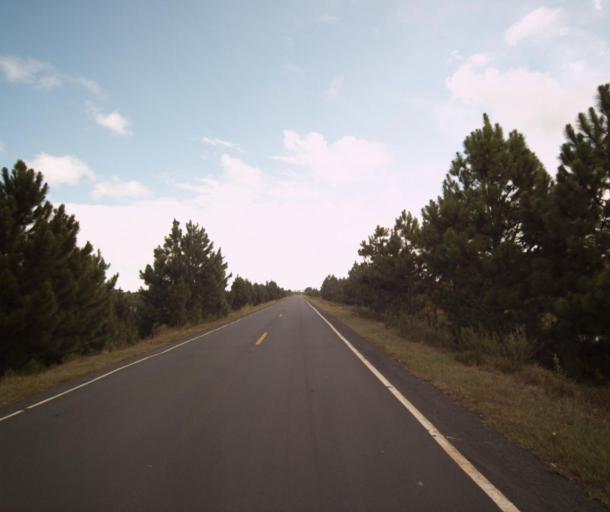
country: BR
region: Rio Grande do Sul
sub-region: Tapes
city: Tapes
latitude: -31.4346
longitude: -51.1930
